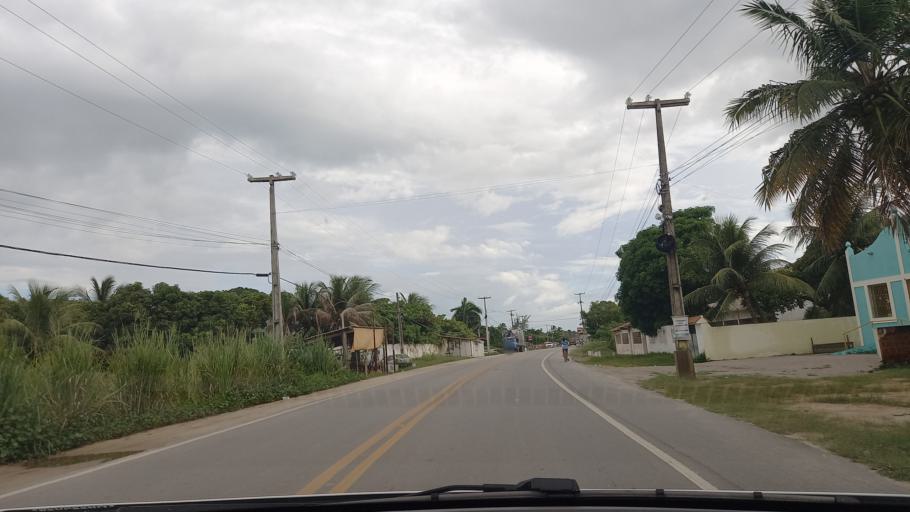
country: BR
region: Pernambuco
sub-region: Sao Jose Da Coroa Grande
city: Sao Jose da Coroa Grande
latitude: -8.9333
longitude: -35.1678
